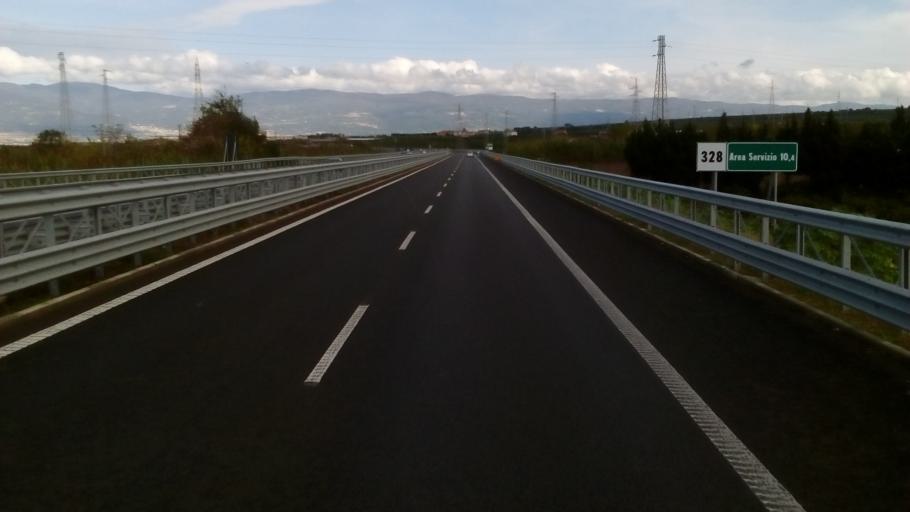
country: IT
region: Calabria
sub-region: Provincia di Catanzaro
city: Acconia
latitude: 38.8531
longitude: 16.2711
